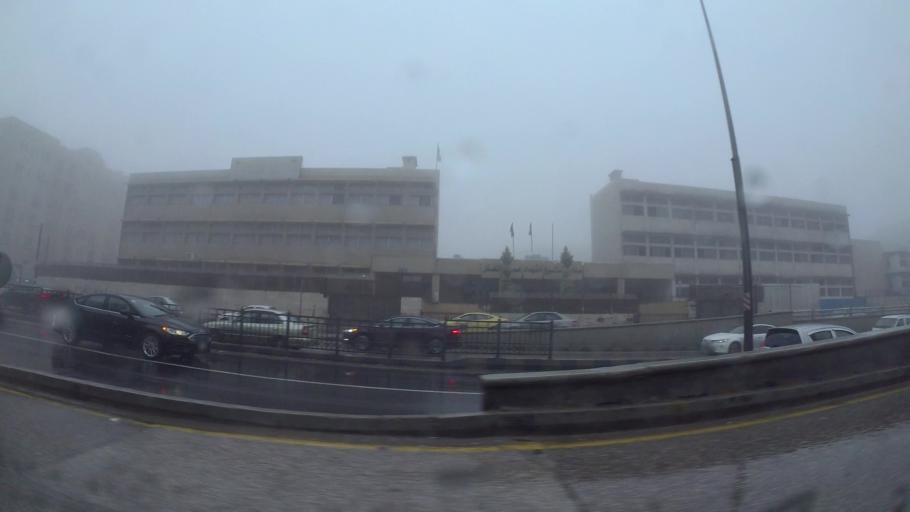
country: JO
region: Amman
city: Al Jubayhah
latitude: 31.9894
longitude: 35.8676
